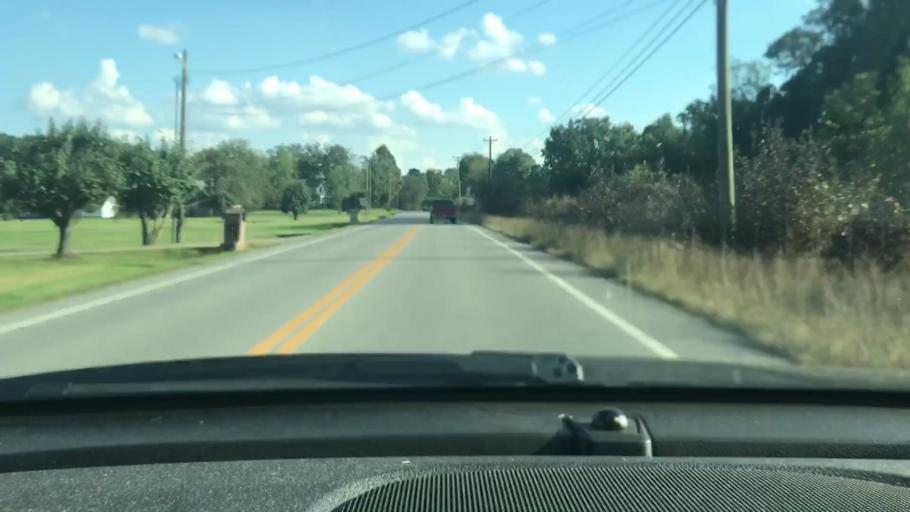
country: US
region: Tennessee
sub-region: Sumner County
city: Shackle Island
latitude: 36.3802
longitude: -86.6197
